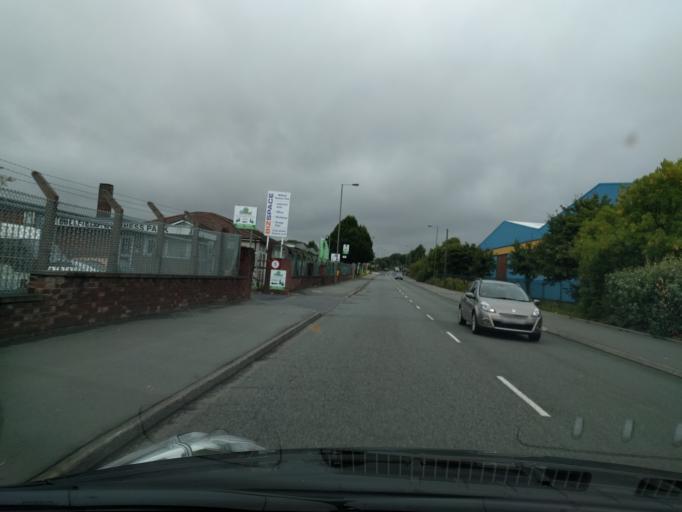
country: GB
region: England
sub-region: Borough of Wigan
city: Ashton in Makerfield
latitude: 53.4760
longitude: -2.6581
